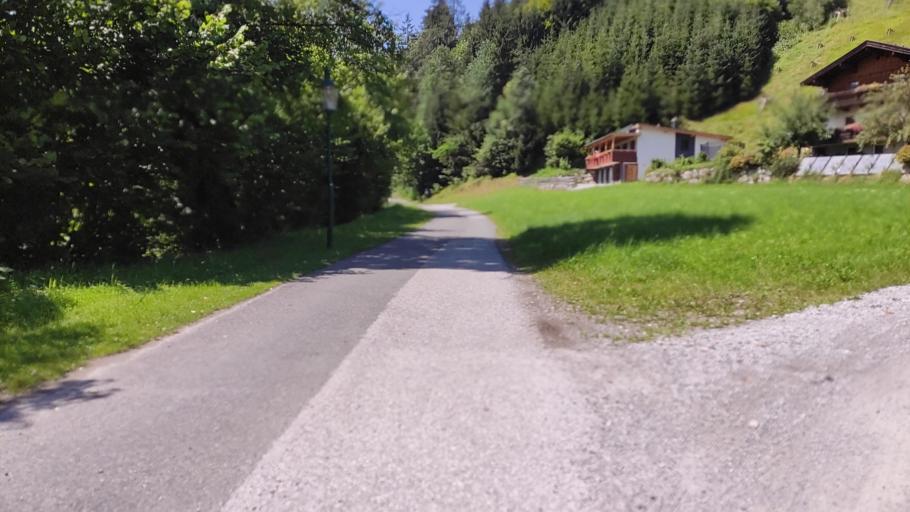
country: AT
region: Salzburg
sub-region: Politischer Bezirk Zell am See
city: Leogang
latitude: 47.4409
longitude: 12.7610
